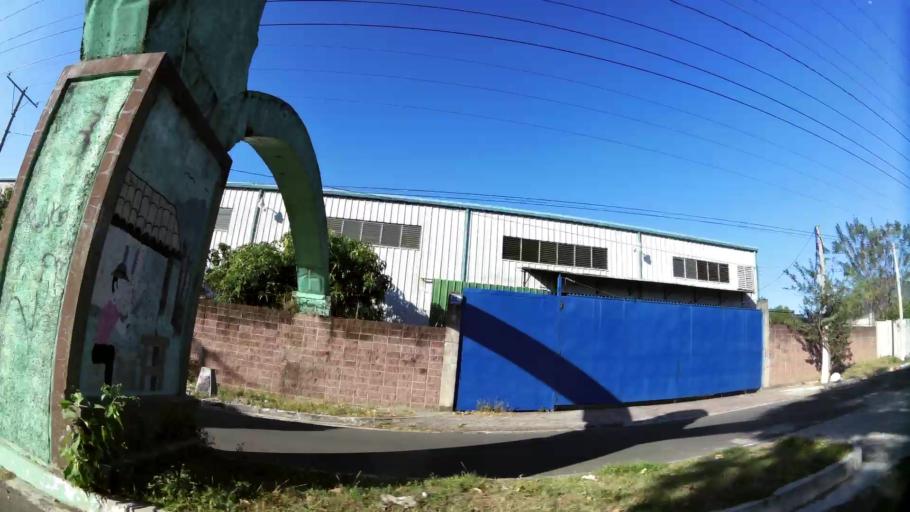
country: SV
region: La Libertad
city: Santa Tecla
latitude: 13.7354
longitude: -89.3592
